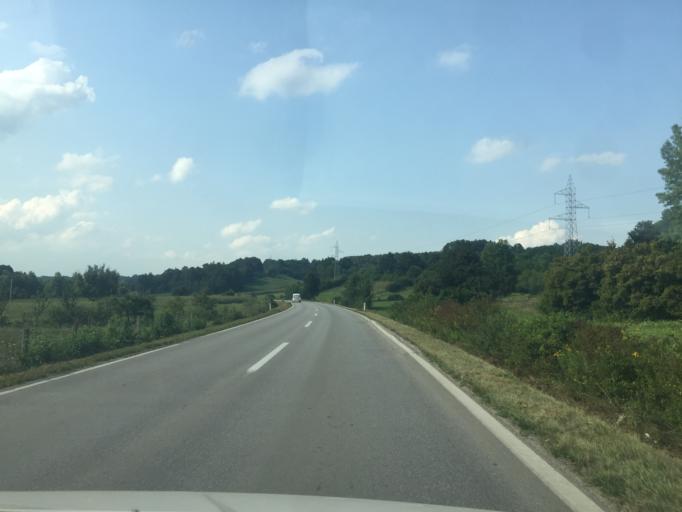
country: BA
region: Federation of Bosnia and Herzegovina
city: Mionica
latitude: 44.8076
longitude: 18.4763
